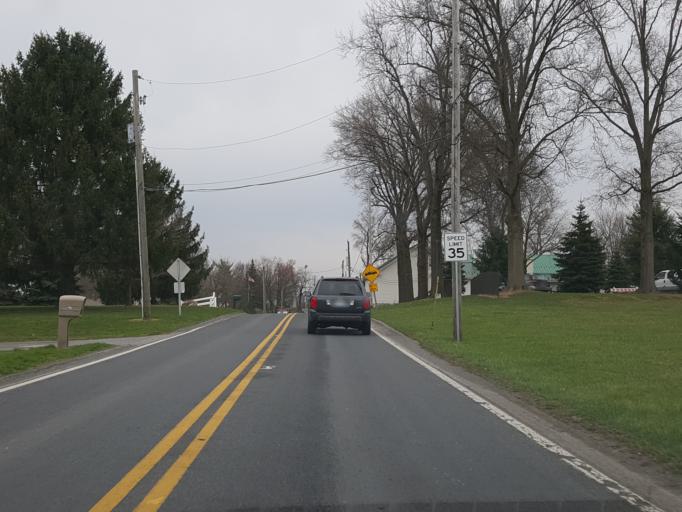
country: US
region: Pennsylvania
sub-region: Lancaster County
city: Rheems
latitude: 40.1580
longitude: -76.5503
